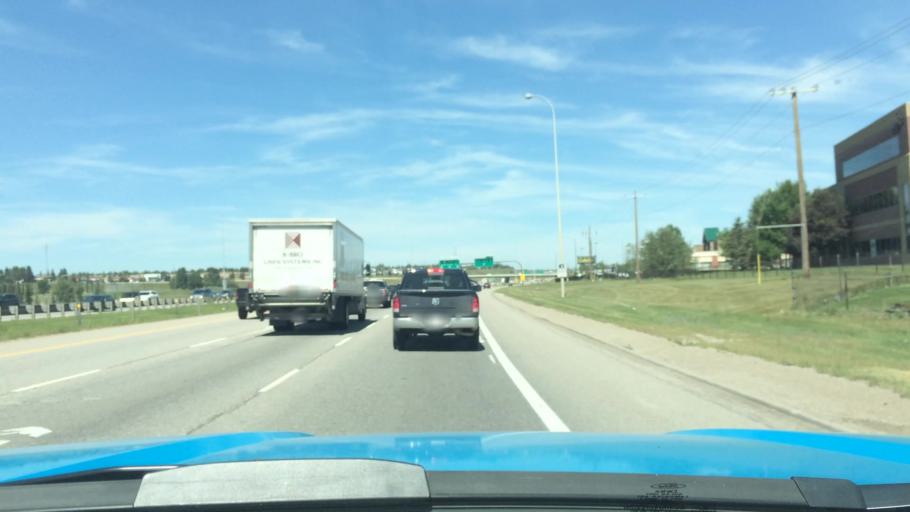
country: CA
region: Alberta
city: Calgary
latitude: 51.1038
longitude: -114.0456
